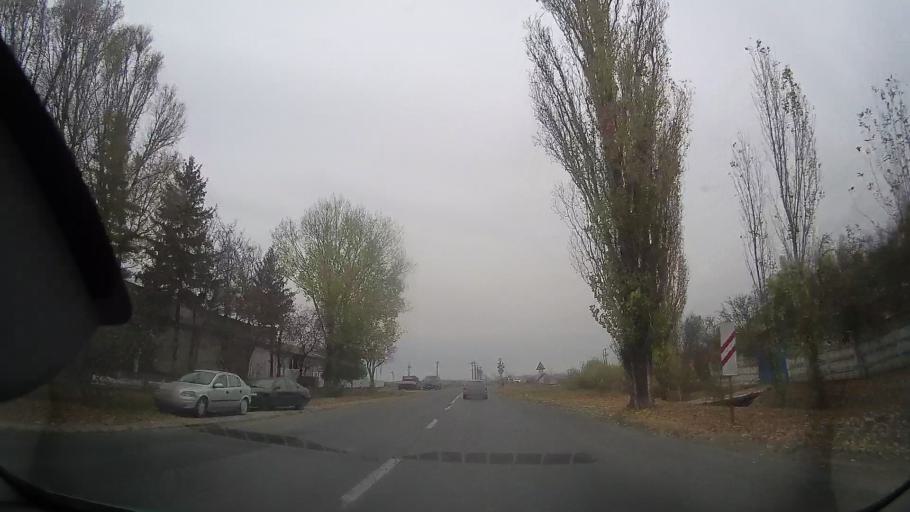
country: RO
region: Ialomita
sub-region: Comuna Slobozia
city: Slobozia
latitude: 44.5789
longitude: 27.3382
